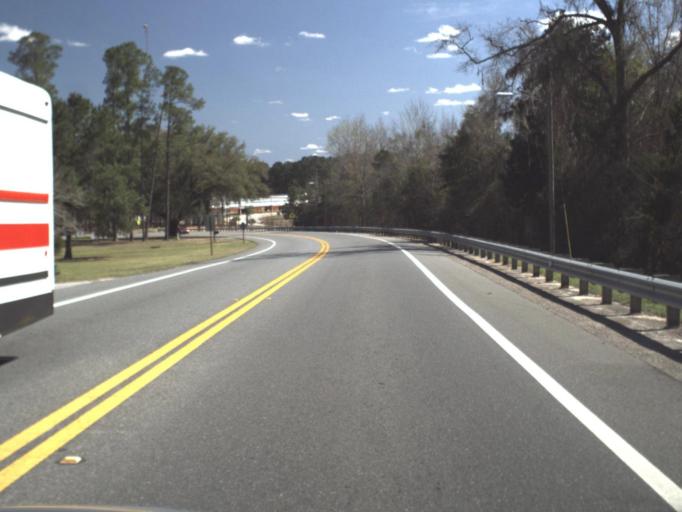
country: US
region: Florida
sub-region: Gadsden County
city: Chattahoochee
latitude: 30.7026
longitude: -84.8374
